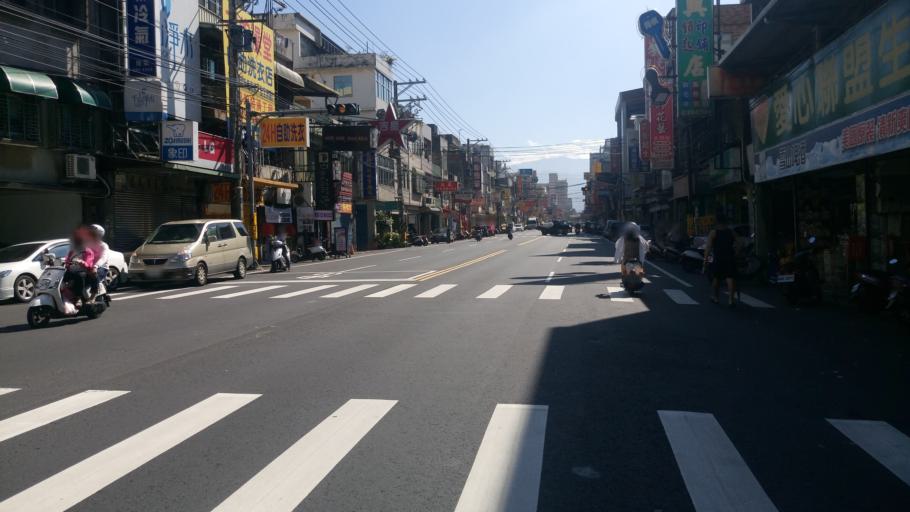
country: TW
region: Taiwan
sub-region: Hsinchu
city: Zhubei
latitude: 24.7460
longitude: 121.0814
